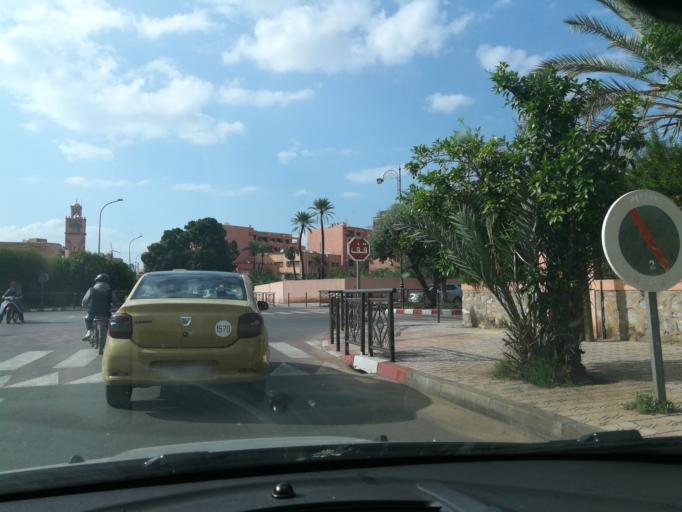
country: MA
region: Marrakech-Tensift-Al Haouz
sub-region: Marrakech
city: Marrakesh
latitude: 31.6285
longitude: -8.0046
